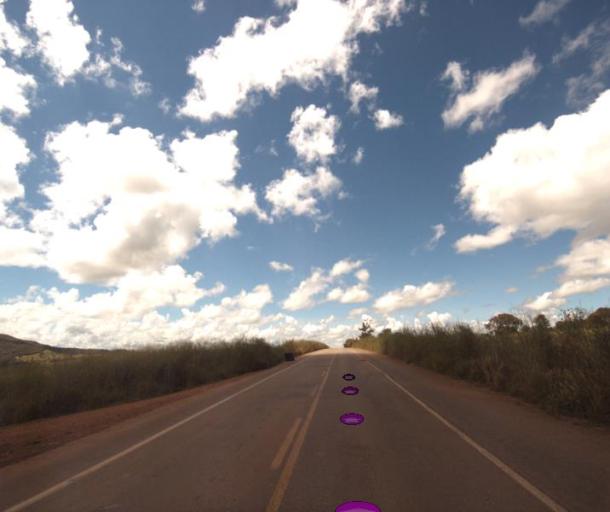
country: BR
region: Goias
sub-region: Pirenopolis
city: Pirenopolis
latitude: -16.0097
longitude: -49.1252
